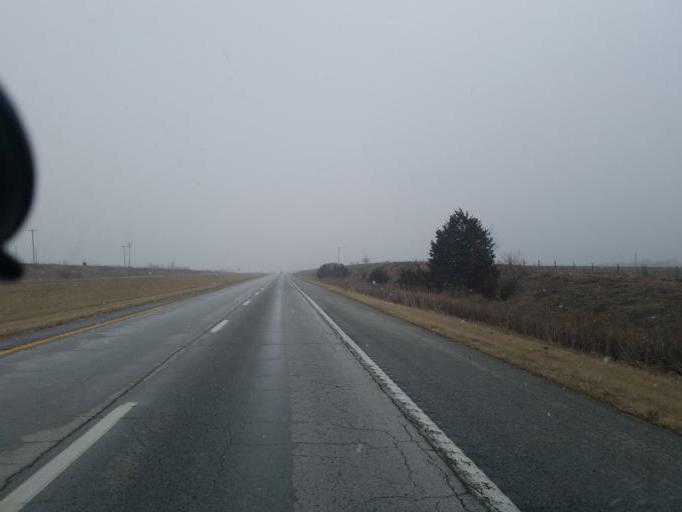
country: US
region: Missouri
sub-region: Macon County
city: La Plata
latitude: 39.9576
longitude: -92.4768
